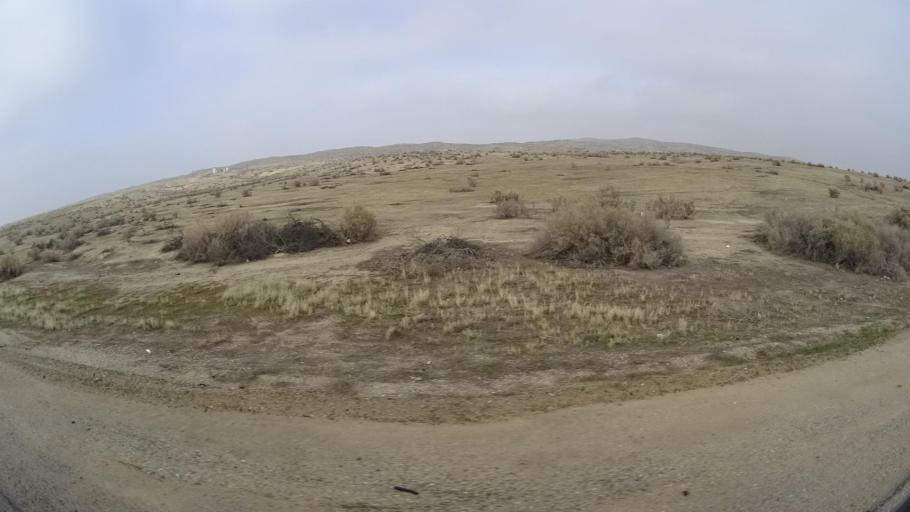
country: US
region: California
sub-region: Kern County
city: South Taft
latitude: 35.1315
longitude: -119.3973
